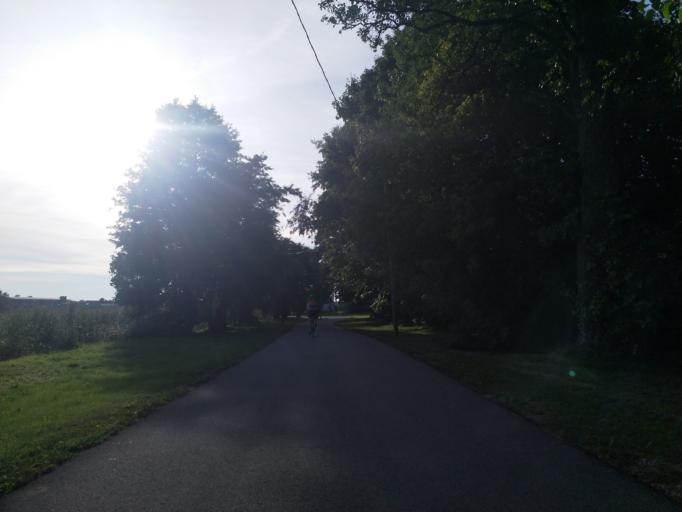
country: EE
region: Paernumaa
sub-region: Paernu linn
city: Parnu
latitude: 58.3825
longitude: 24.5395
